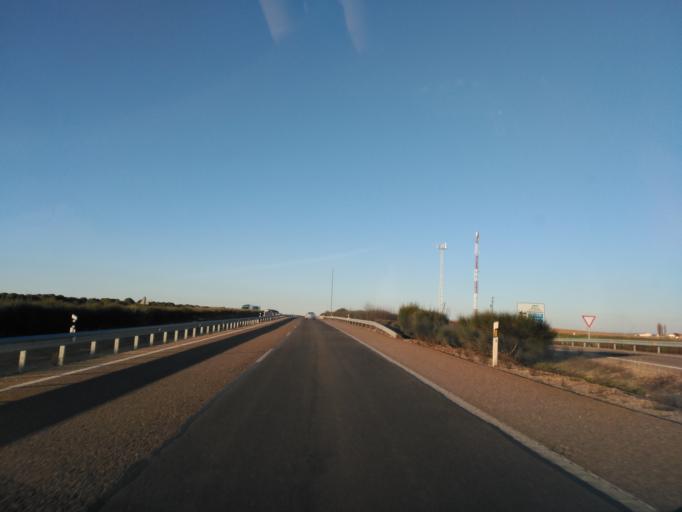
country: ES
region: Castille and Leon
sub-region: Provincia de Valladolid
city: Alaejos
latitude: 41.3007
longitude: -5.2302
